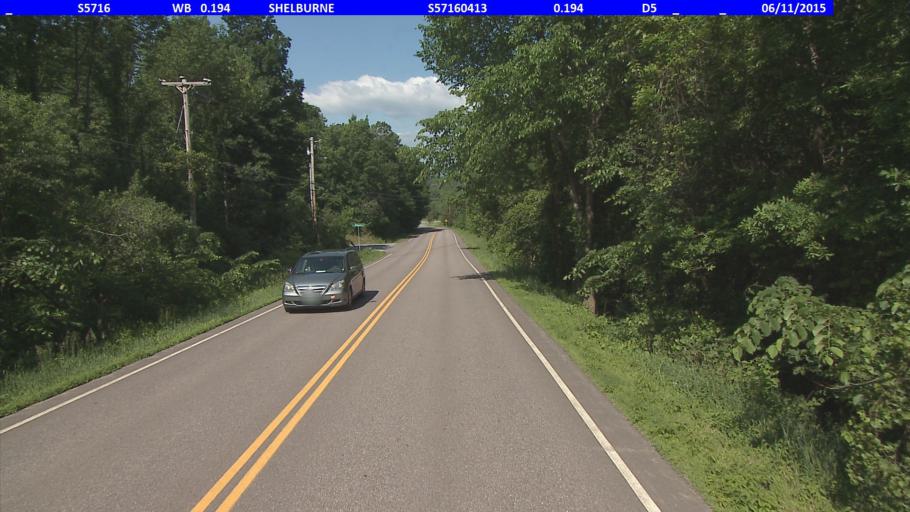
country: US
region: Vermont
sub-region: Chittenden County
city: South Burlington
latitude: 44.3728
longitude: -73.2079
